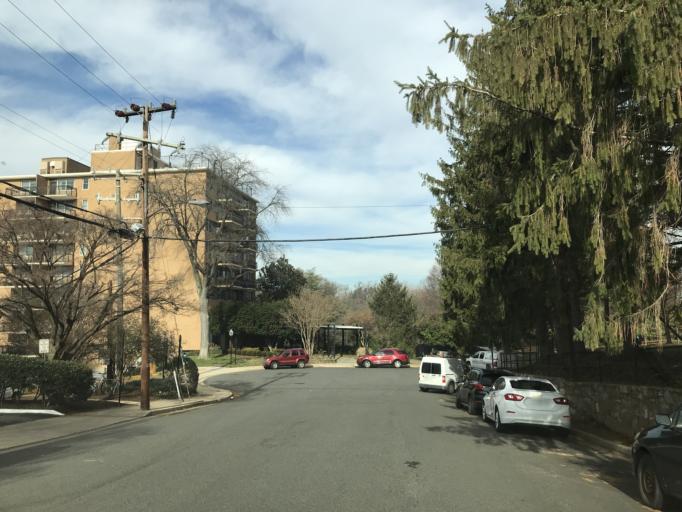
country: US
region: Virginia
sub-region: Arlington County
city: Arlington
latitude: 38.8972
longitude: -77.0890
